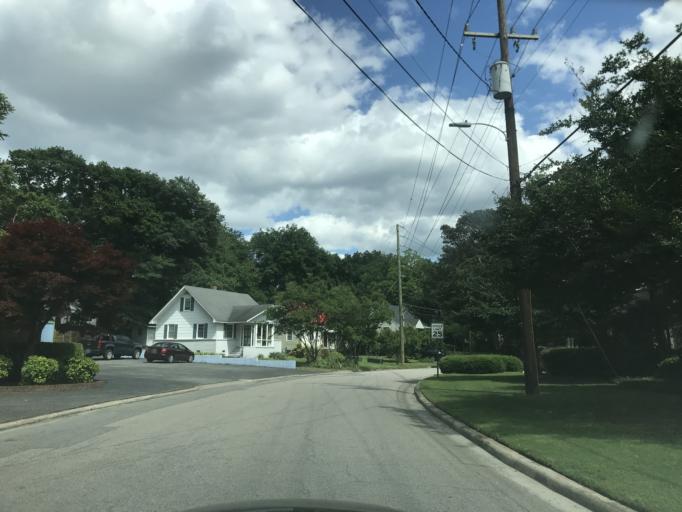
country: US
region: North Carolina
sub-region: Wake County
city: Raleigh
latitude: 35.8056
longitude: -78.6276
